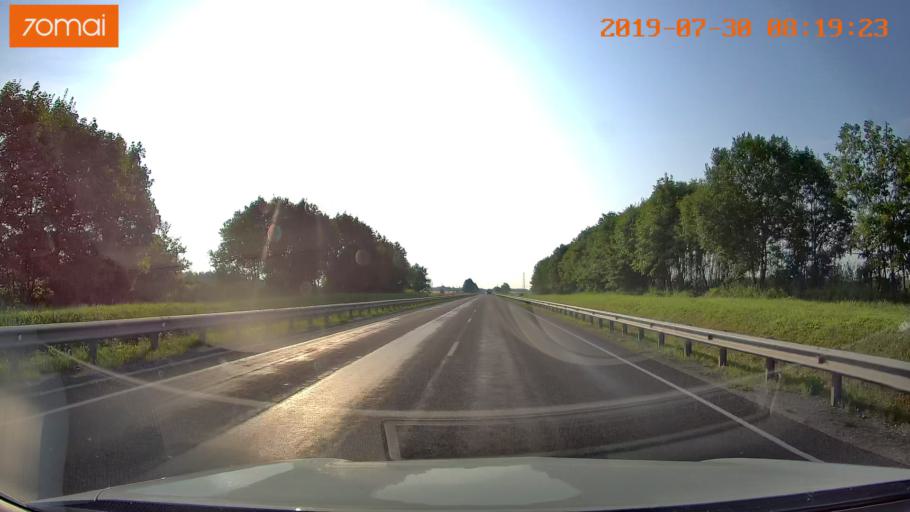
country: RU
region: Kaliningrad
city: Zheleznodorozhnyy
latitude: 54.6288
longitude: 21.4899
